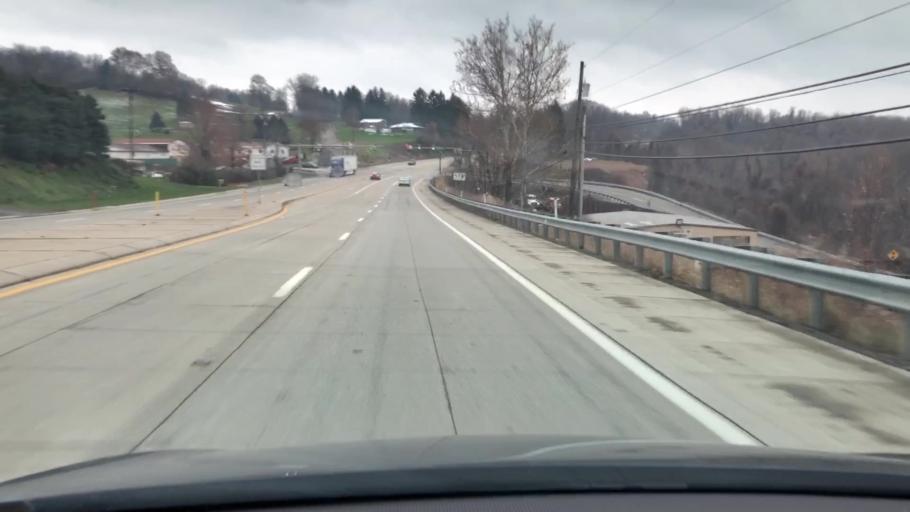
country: US
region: Pennsylvania
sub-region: Fayette County
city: Dunbar
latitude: 39.9855
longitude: -79.6302
